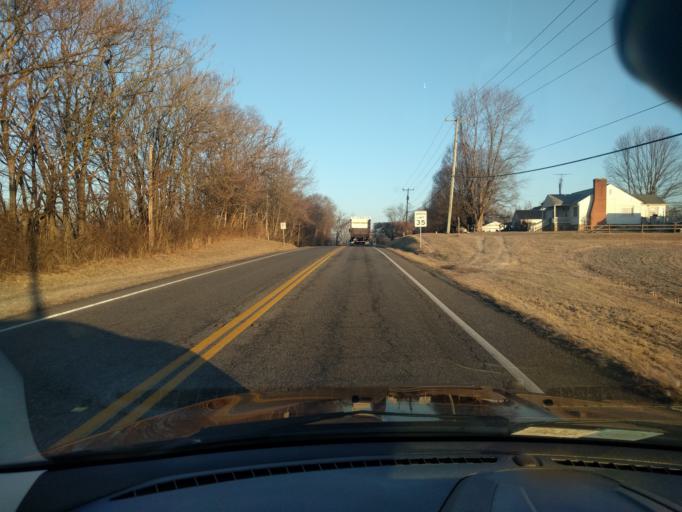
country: US
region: Virginia
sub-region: Rockingham County
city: Bridgewater
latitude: 38.3491
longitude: -78.9434
